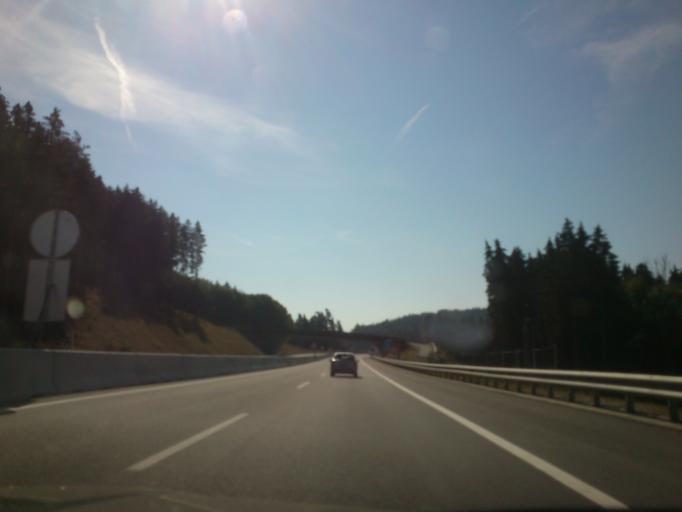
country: AT
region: Upper Austria
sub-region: Politischer Bezirk Freistadt
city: Freistadt
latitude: 48.5228
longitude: 14.5092
